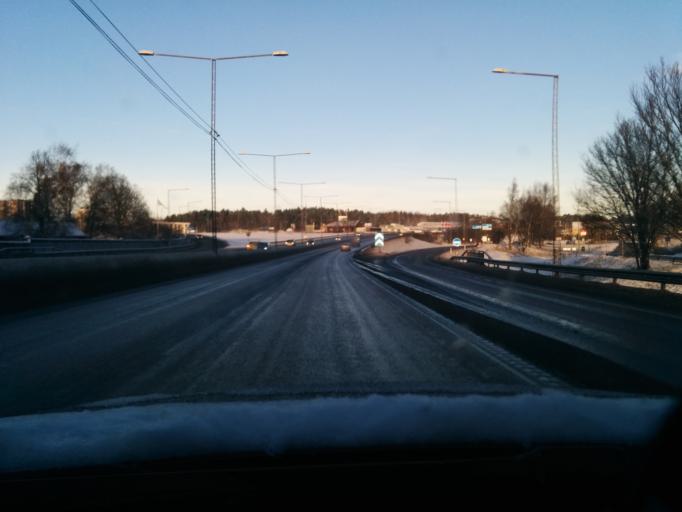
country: SE
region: Stockholm
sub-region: Danderyds Kommun
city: Djursholm
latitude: 59.4069
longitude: 18.0354
